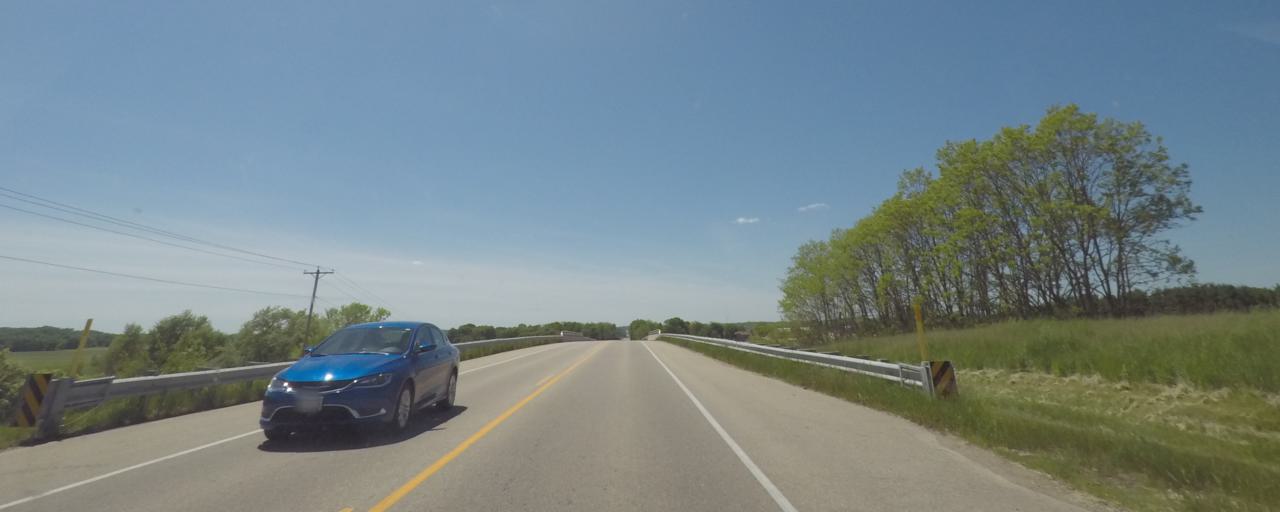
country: US
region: Wisconsin
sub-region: Dane County
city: Oregon
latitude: 42.9502
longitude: -89.3898
